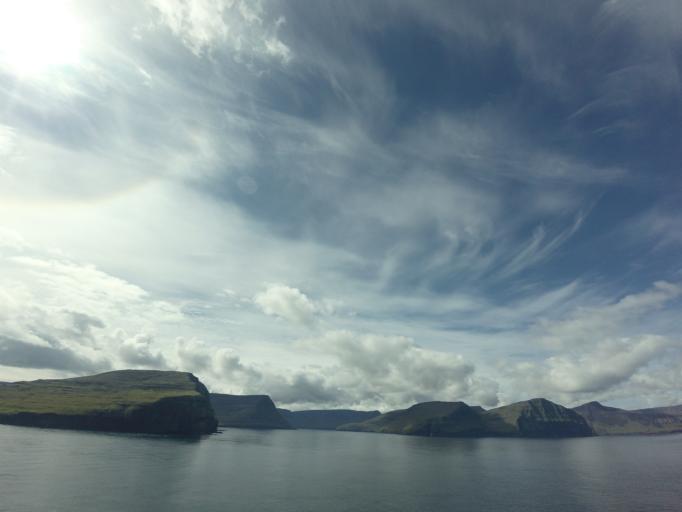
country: FO
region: Nordoyar
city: Klaksvik
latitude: 62.3215
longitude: -6.3252
